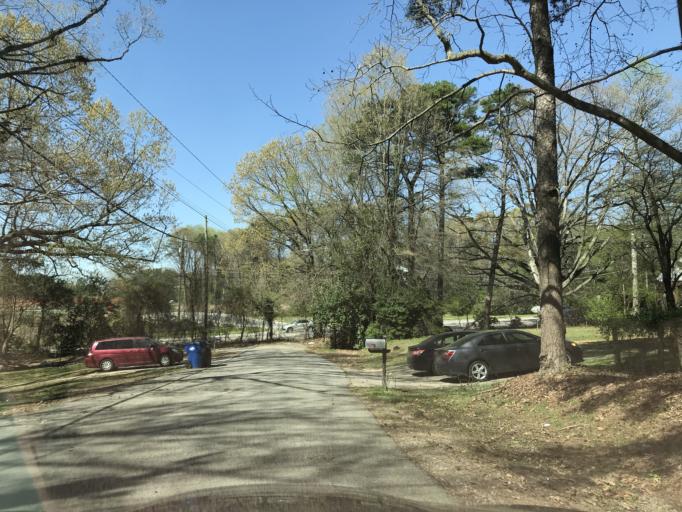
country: US
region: North Carolina
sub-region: Wake County
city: West Raleigh
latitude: 35.7831
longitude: -78.6971
